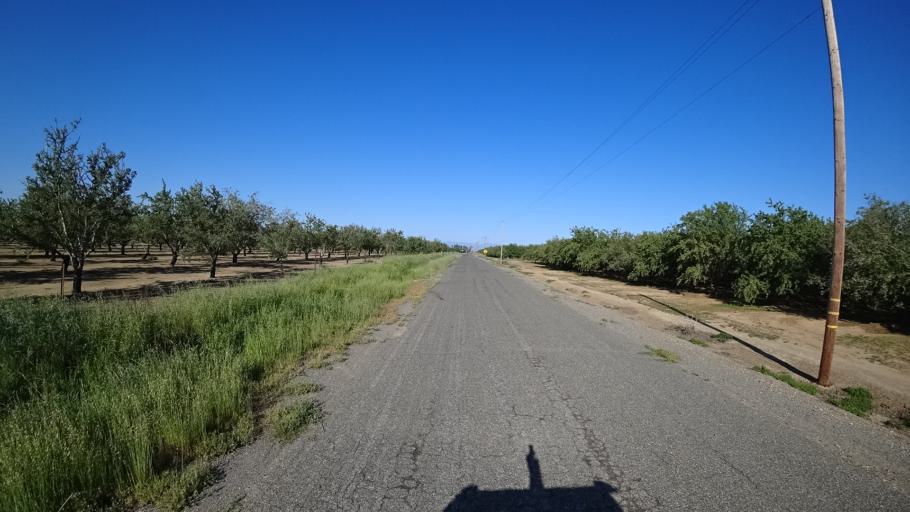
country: US
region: California
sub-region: Glenn County
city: Hamilton City
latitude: 39.6959
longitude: -122.0997
